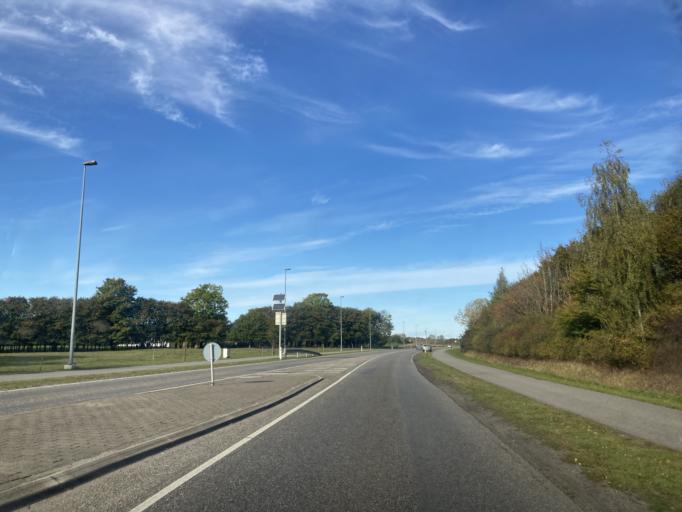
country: DK
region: Capital Region
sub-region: Vallensbaek Kommune
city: Vallensbaek
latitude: 55.6332
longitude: 12.3765
